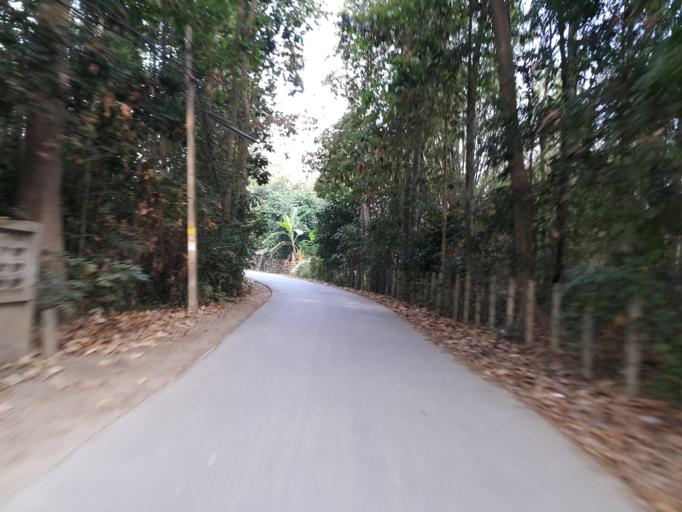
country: TH
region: Chiang Mai
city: San Sai
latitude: 18.8265
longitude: 99.1042
